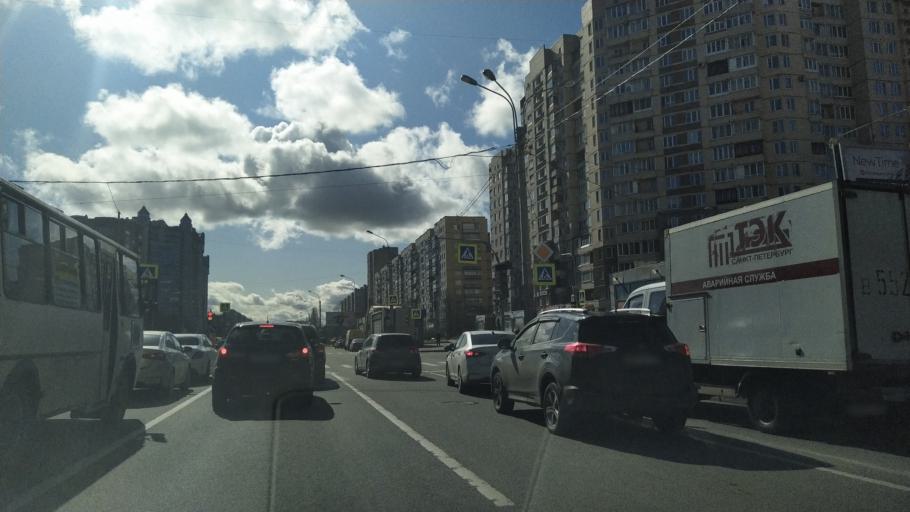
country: RU
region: St.-Petersburg
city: Ozerki
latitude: 60.0476
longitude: 30.3307
